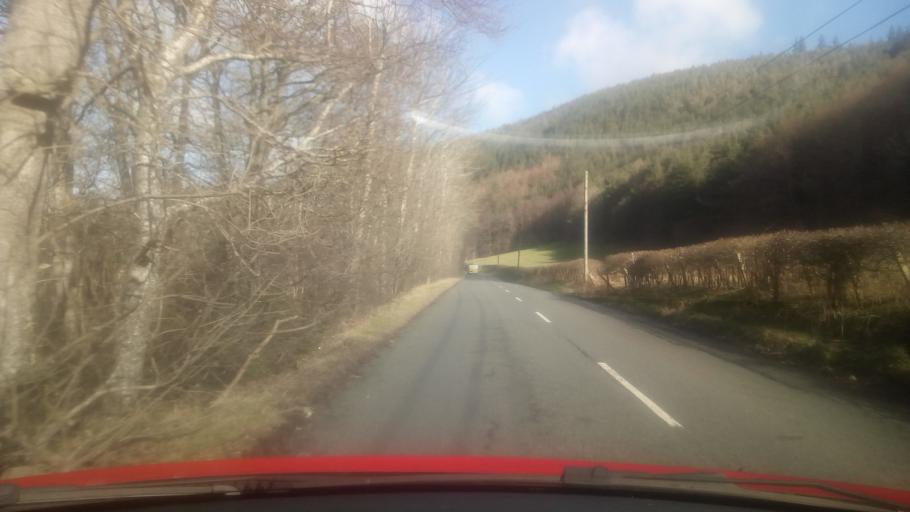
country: GB
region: Scotland
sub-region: The Scottish Borders
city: Selkirk
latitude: 55.5946
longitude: -2.8662
